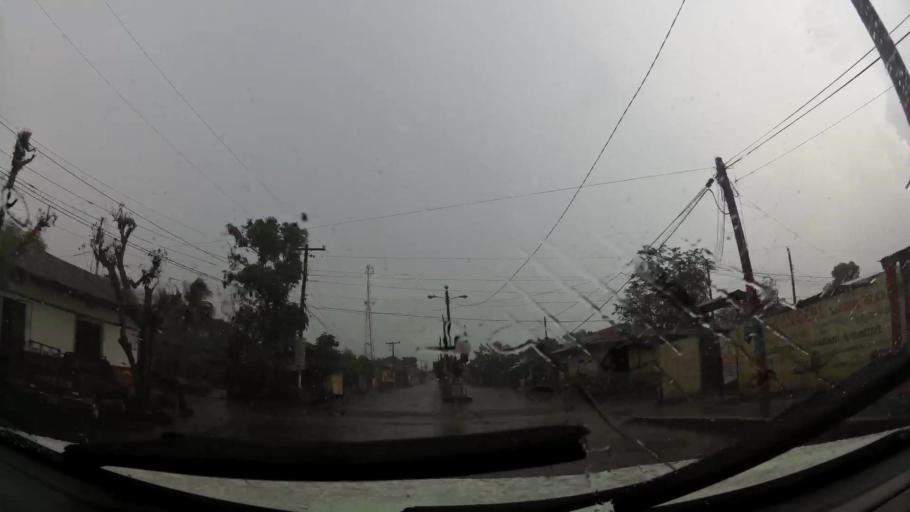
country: NI
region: Leon
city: Telica
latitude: 12.5215
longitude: -86.8629
